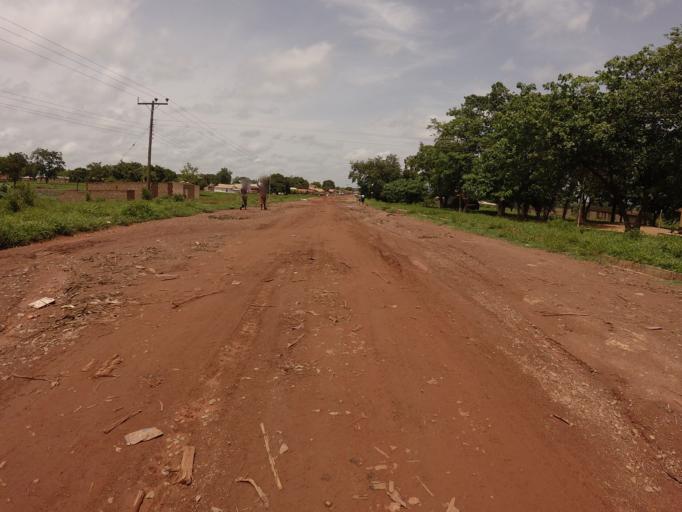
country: GH
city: Kpandae
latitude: 8.6106
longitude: 0.2324
